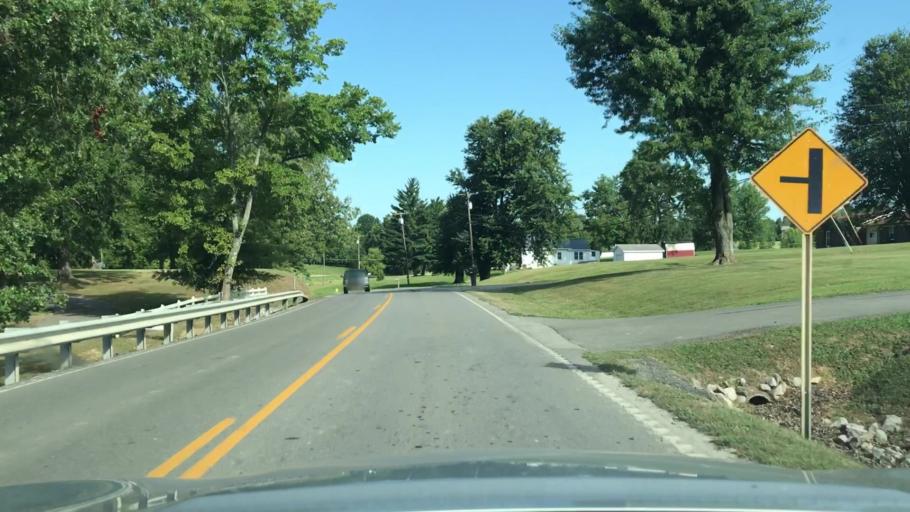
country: US
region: Kentucky
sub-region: Muhlenberg County
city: Greenville
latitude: 37.1861
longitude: -87.1618
